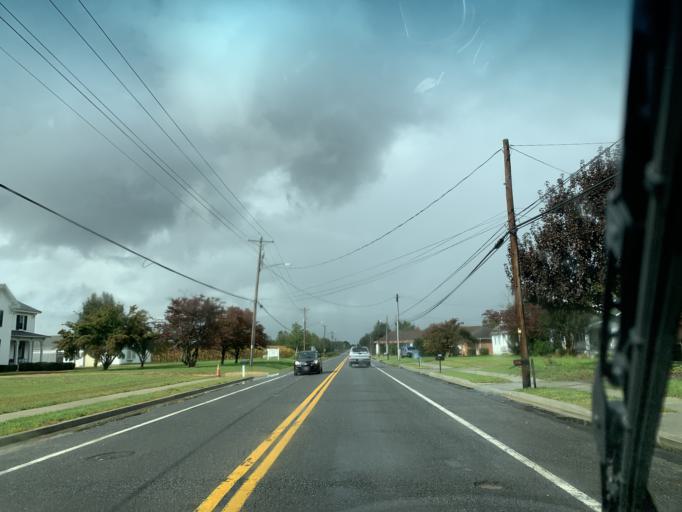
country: US
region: Maryland
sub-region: Queen Anne's County
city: Kingstown
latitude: 39.1902
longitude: -75.8598
